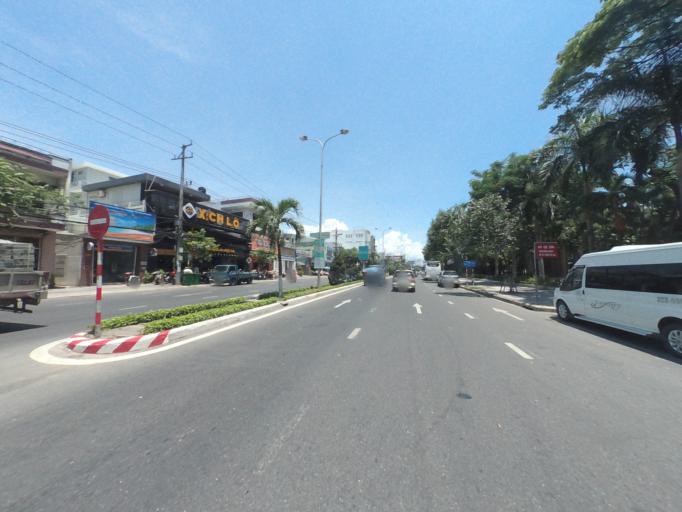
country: VN
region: Da Nang
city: Thanh Khe
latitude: 16.0624
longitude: 108.2042
